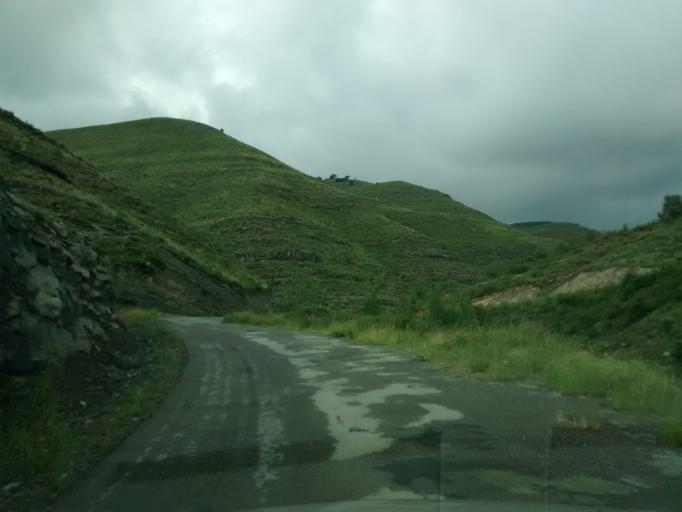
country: ES
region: La Rioja
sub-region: Provincia de La Rioja
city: San Roman de Cameros
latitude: 42.2195
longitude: -2.4629
